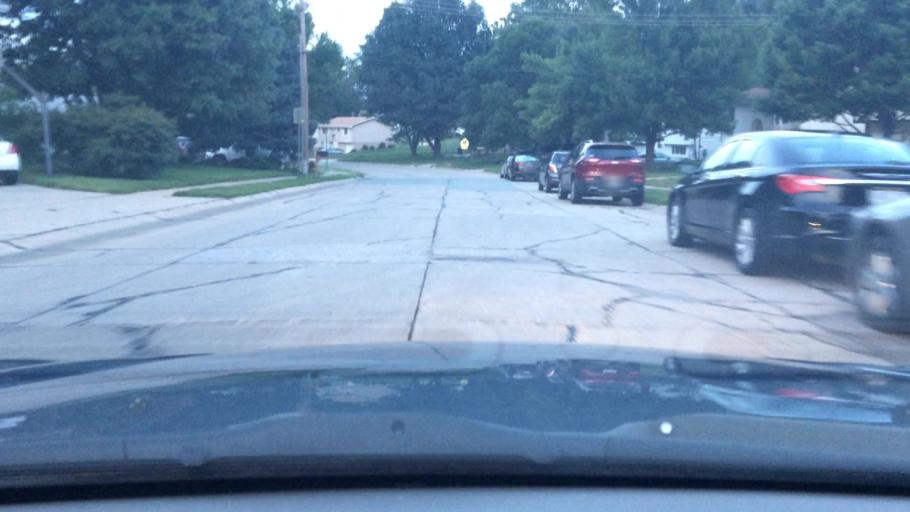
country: US
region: Nebraska
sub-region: Sarpy County
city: La Vista
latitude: 41.1839
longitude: -96.0530
